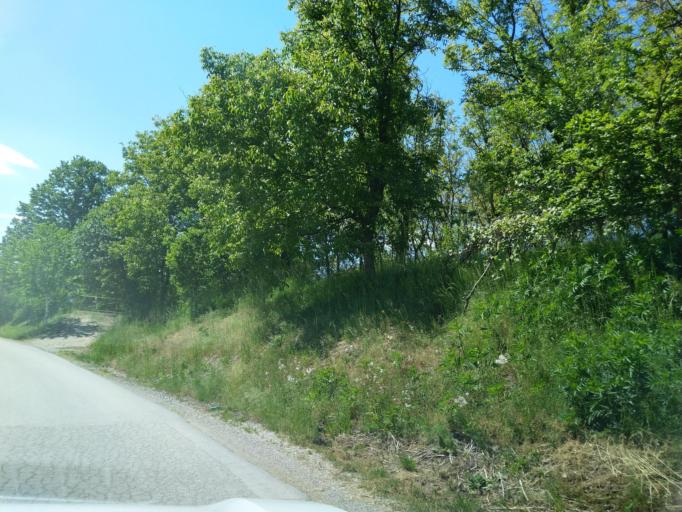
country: RS
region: Central Serbia
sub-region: Zlatiborski Okrug
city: Uzice
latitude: 43.8580
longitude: 19.9139
